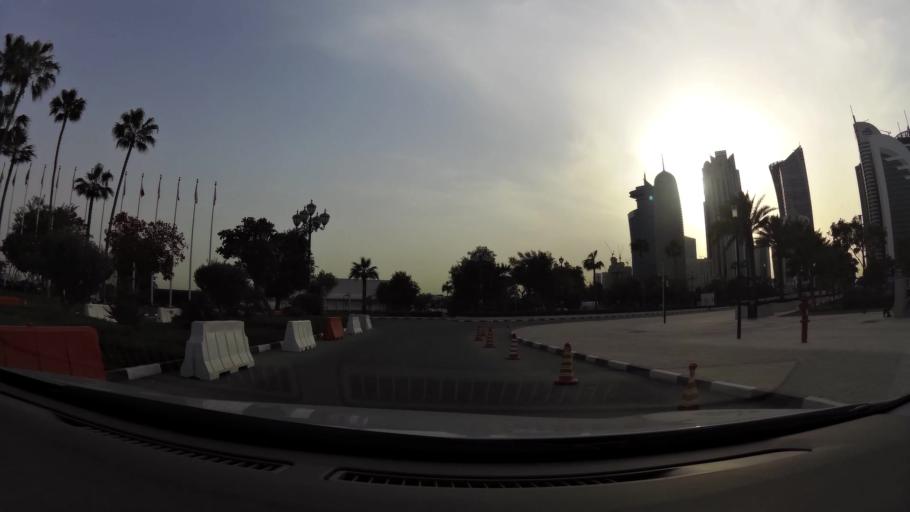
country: QA
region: Baladiyat ad Dawhah
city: Doha
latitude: 25.3188
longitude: 51.5351
